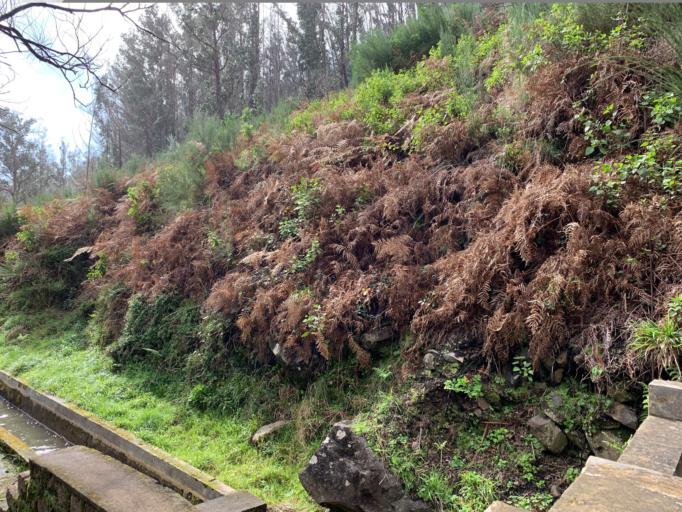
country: PT
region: Madeira
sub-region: Calheta
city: Estreito da Calheta
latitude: 32.7589
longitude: -17.1671
